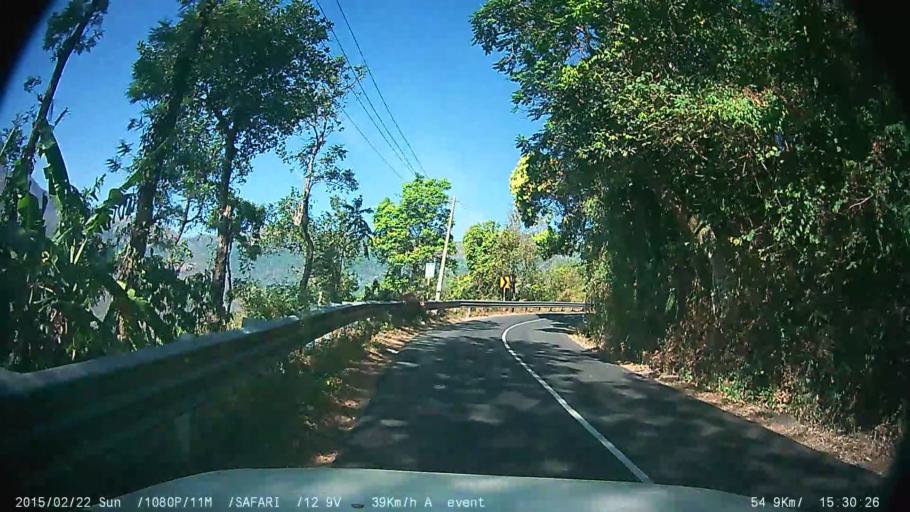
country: IN
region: Kerala
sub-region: Kottayam
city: Erattupetta
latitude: 9.5599
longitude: 76.9538
